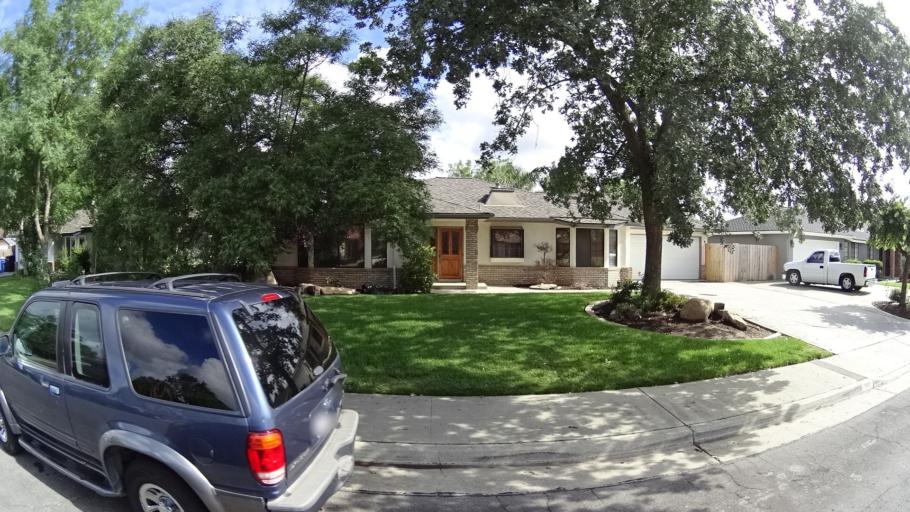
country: US
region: California
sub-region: Kings County
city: Lucerne
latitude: 36.3629
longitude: -119.6475
